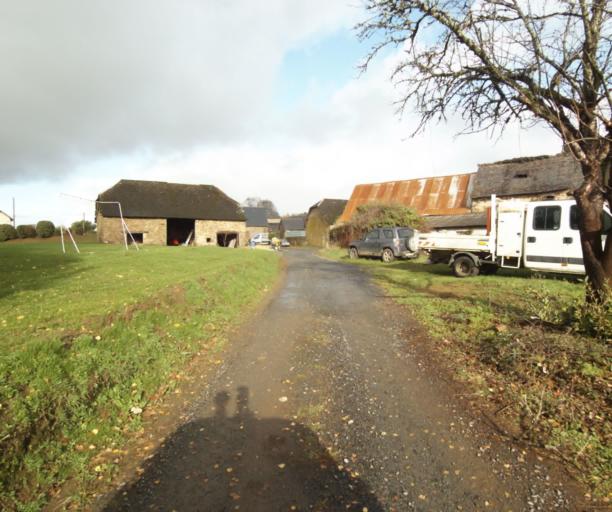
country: FR
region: Limousin
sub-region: Departement de la Correze
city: Sainte-Fereole
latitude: 45.2313
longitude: 1.6342
